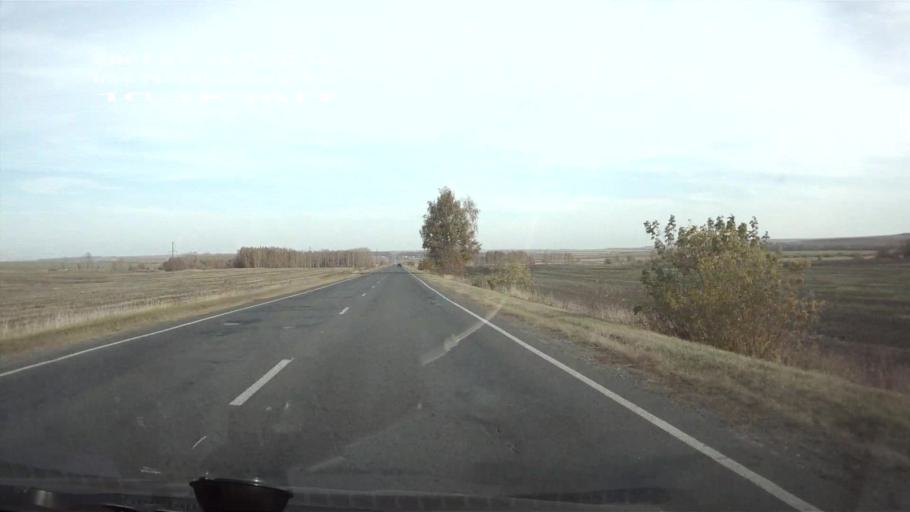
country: RU
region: Mordoviya
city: Atyashevo
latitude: 54.5403
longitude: 45.9346
